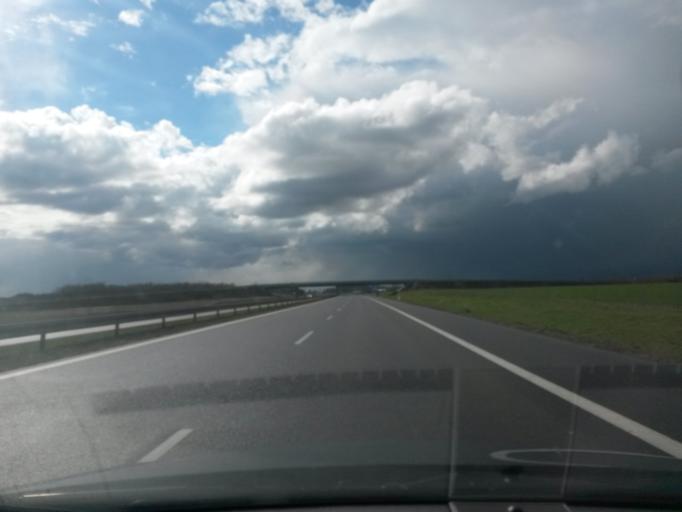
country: PL
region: Greater Poland Voivodeship
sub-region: Powiat wrzesinski
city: Nekla
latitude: 52.3189
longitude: 17.4305
